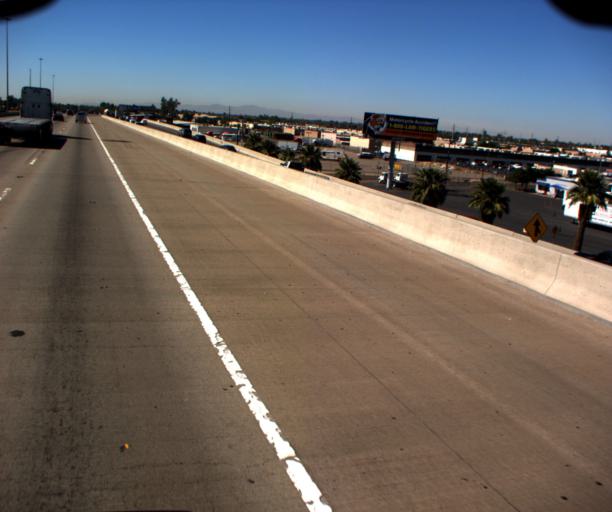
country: US
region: Arizona
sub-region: Maricopa County
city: Phoenix
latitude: 33.4620
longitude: -112.1115
